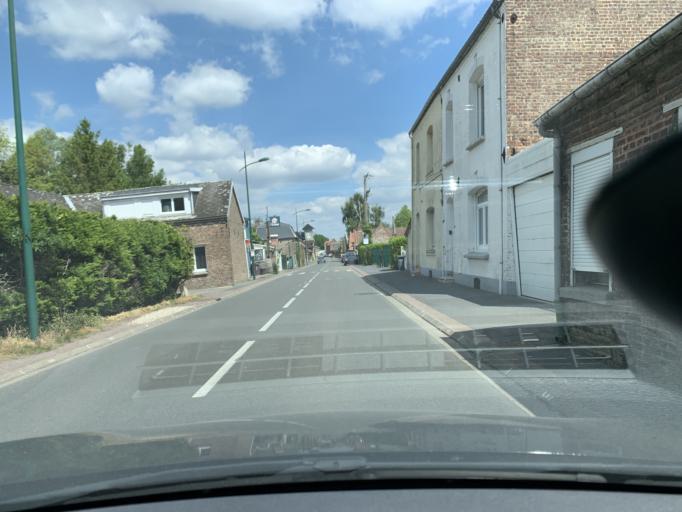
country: FR
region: Nord-Pas-de-Calais
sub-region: Departement du Nord
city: Arleux
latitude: 50.2744
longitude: 3.1007
